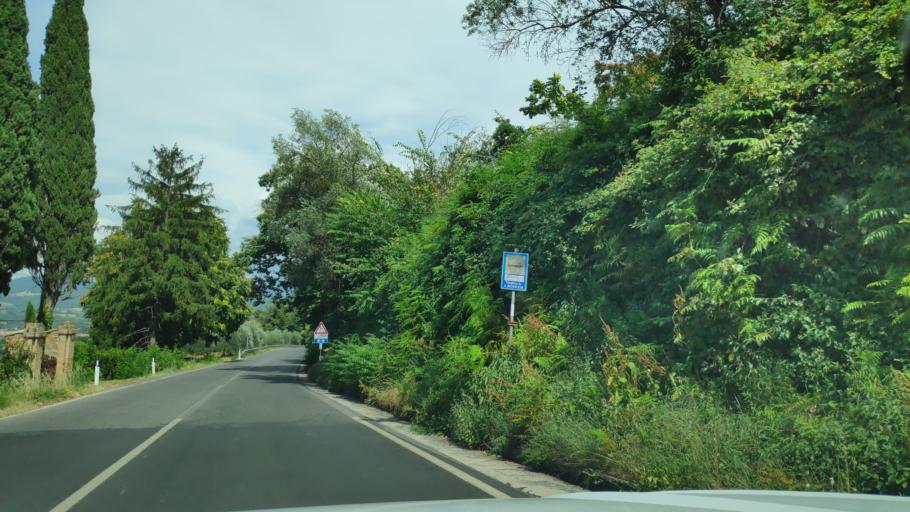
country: IT
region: Umbria
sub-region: Provincia di Terni
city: Orvieto
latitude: 42.7220
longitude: 12.1046
